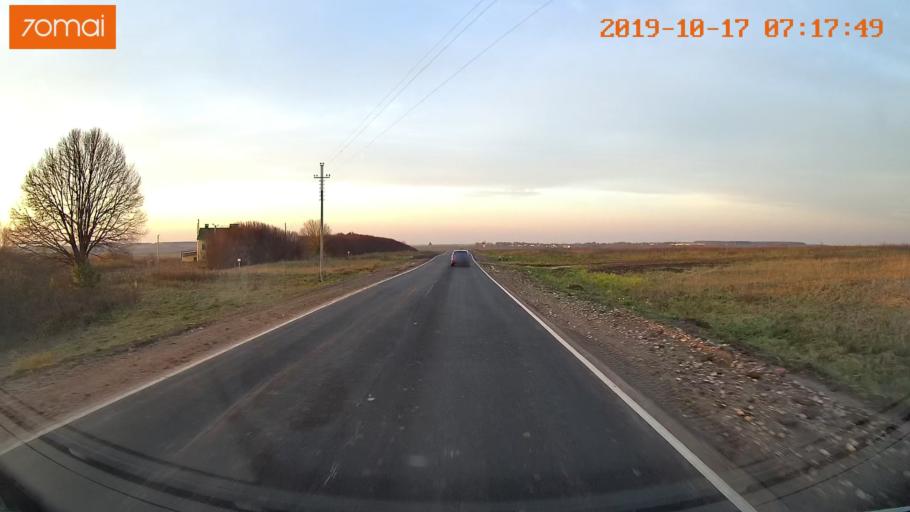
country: RU
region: Ivanovo
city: Gavrilov Posad
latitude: 56.3596
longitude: 40.2265
